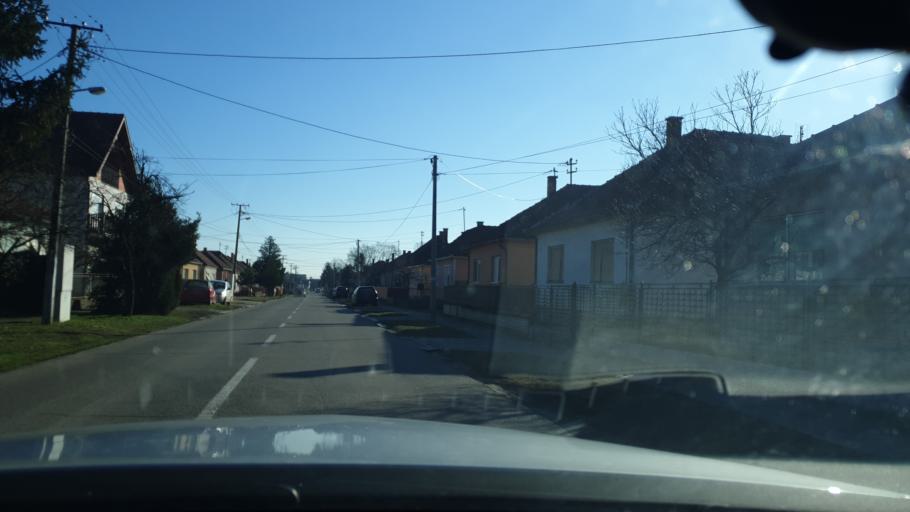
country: RS
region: Autonomna Pokrajina Vojvodina
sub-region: Sremski Okrug
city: Ruma
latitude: 45.0184
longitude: 19.8167
